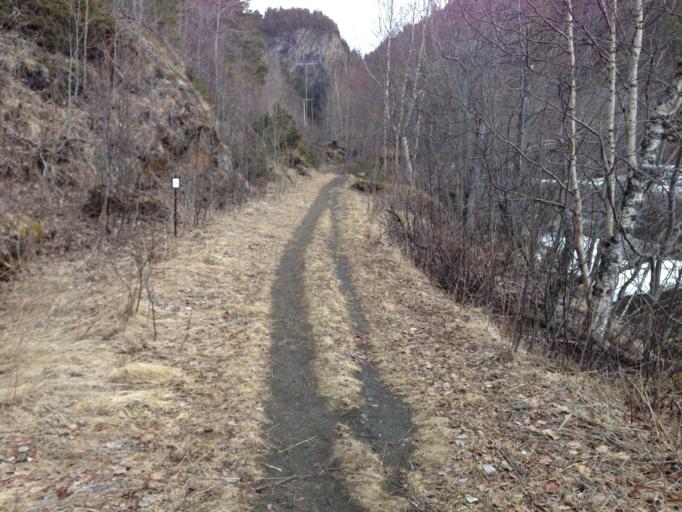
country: NO
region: Nordland
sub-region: Saltdal
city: Rognan
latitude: 66.8149
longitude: 15.4115
